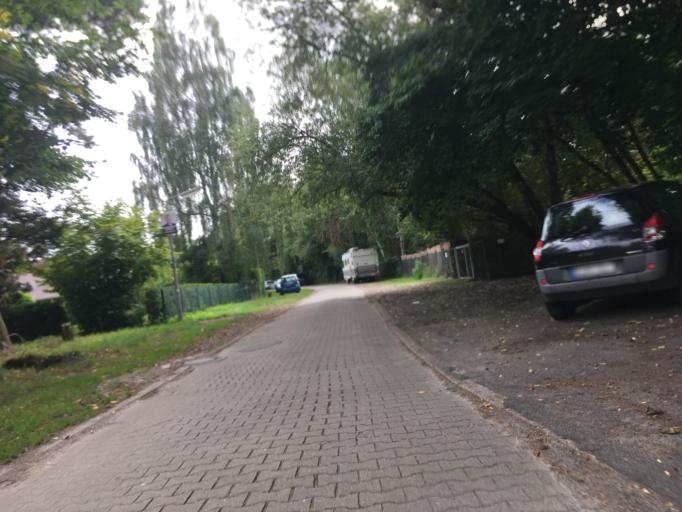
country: DE
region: Berlin
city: Konradshohe
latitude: 52.6080
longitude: 13.2209
